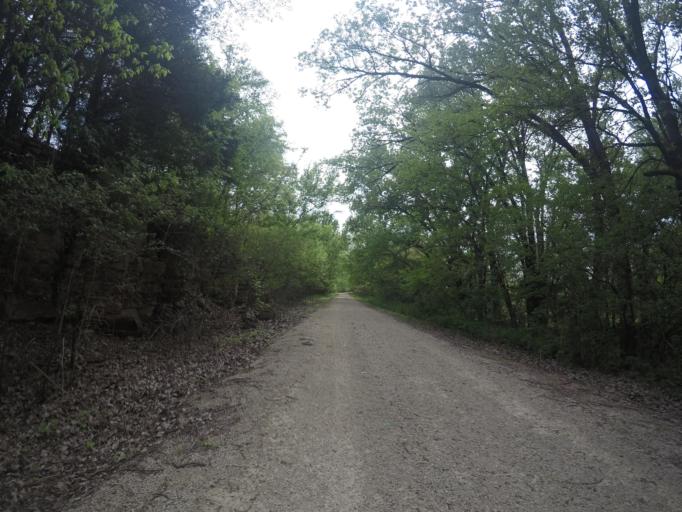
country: US
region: Nebraska
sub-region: Gage County
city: Wymore
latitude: 40.0188
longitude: -96.5906
